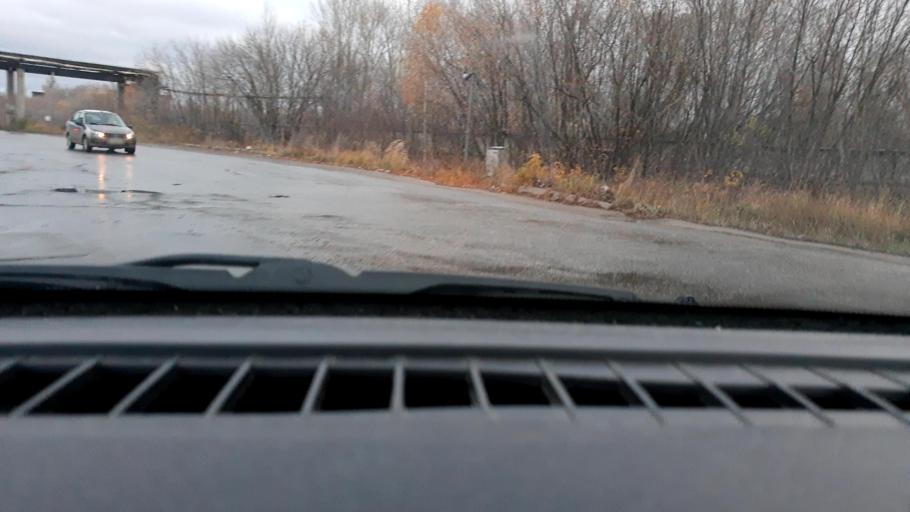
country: RU
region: Nizjnij Novgorod
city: Nizhniy Novgorod
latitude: 56.2391
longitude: 43.9065
